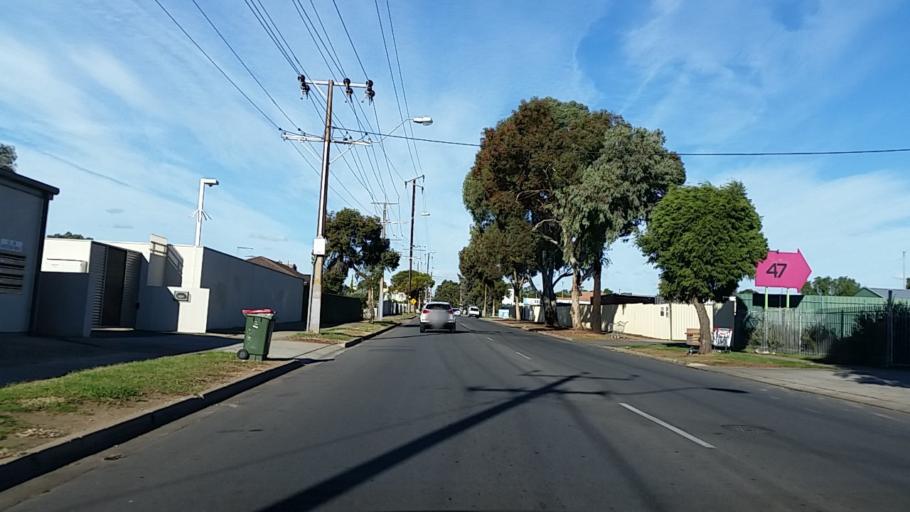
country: AU
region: South Australia
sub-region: Playford
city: Smithfield
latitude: -34.6804
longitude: 138.6852
